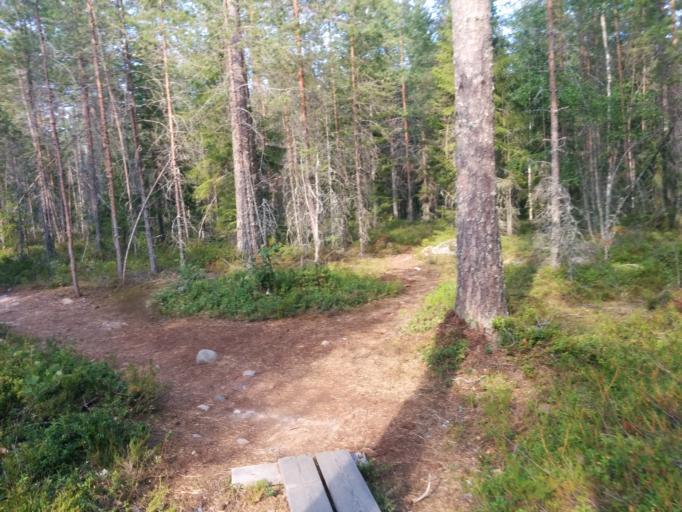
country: SE
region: Vaesterbotten
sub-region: Umea Kommun
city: Ersmark
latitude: 63.8172
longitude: 20.3612
